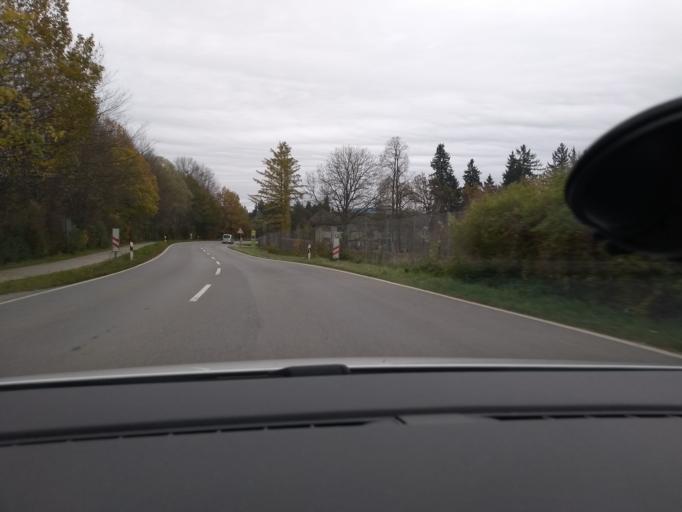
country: DE
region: Bavaria
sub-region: Upper Bavaria
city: Stephanskirchen
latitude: 47.8436
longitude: 12.1621
